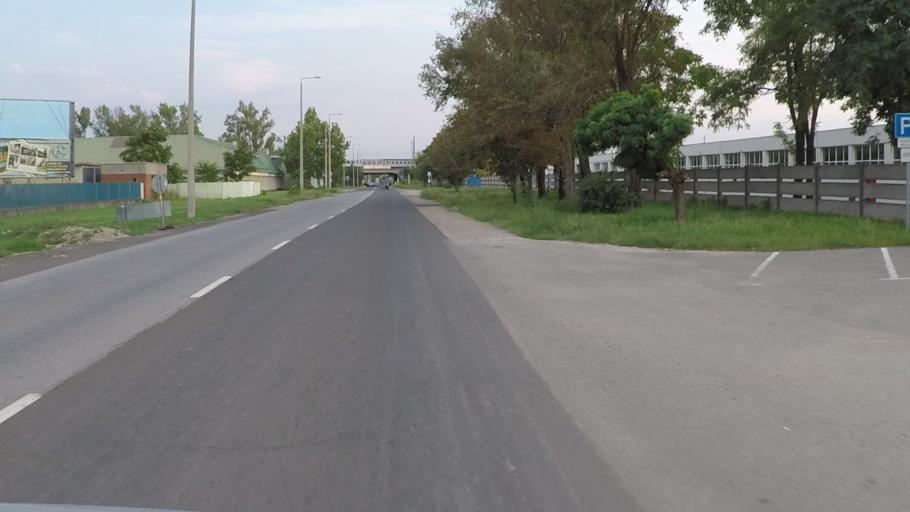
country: HU
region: Jasz-Nagykun-Szolnok
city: Szolnok
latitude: 47.1844
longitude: 20.1553
